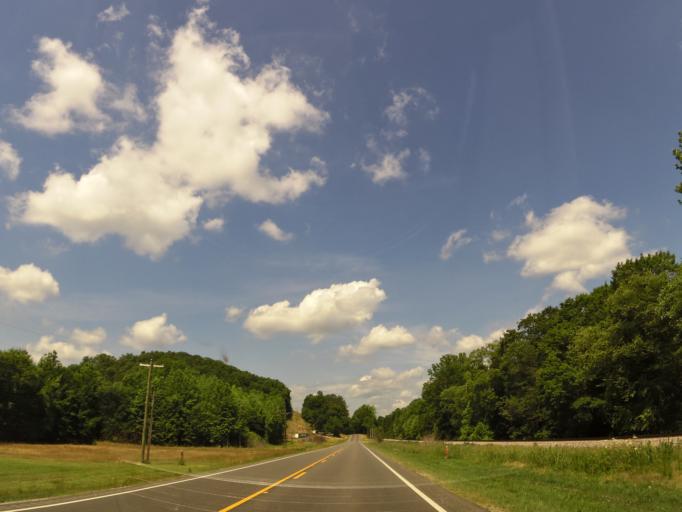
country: US
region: Alabama
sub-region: Marion County
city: Guin
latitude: 33.9547
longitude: -87.9571
